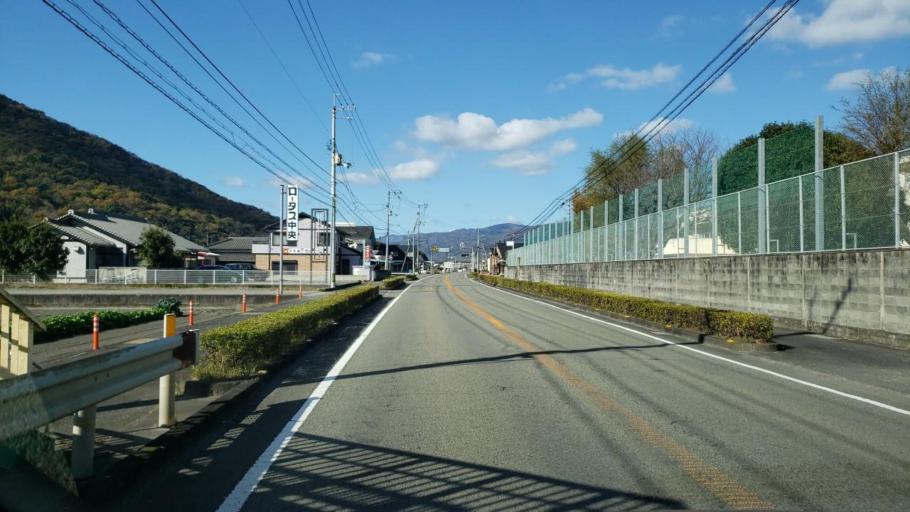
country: JP
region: Tokushima
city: Wakimachi
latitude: 34.0610
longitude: 134.2092
